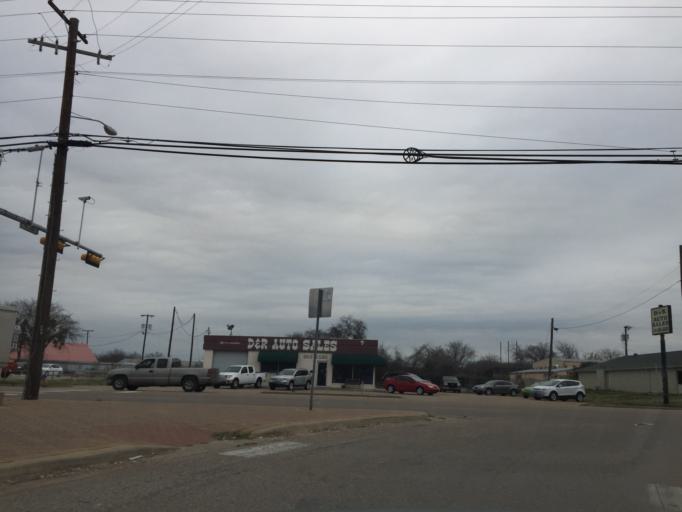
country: US
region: Texas
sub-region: Coryell County
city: Gatesville
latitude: 31.4345
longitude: -97.7318
